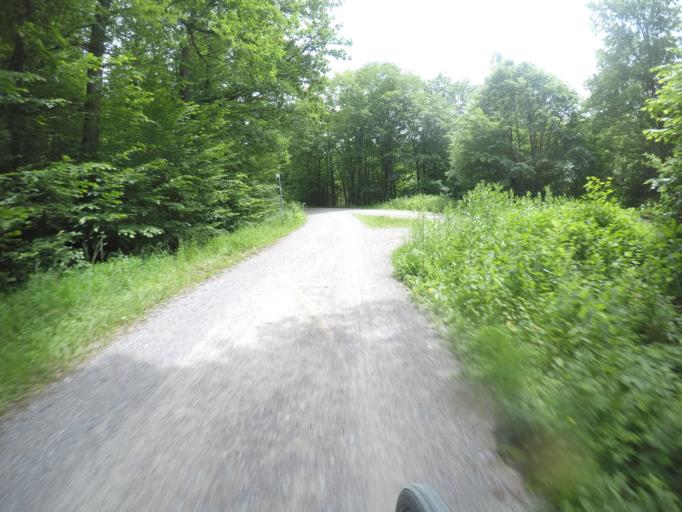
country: DE
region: Baden-Wuerttemberg
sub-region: Regierungsbezirk Stuttgart
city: Hildrizhausen
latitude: 48.5902
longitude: 8.9488
